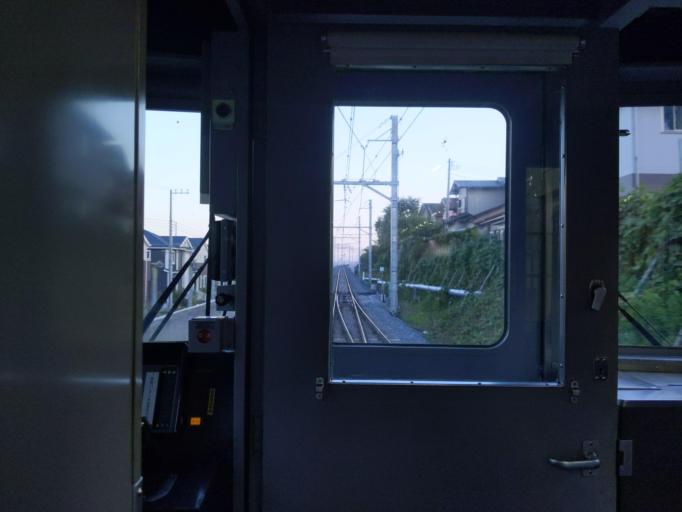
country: JP
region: Chiba
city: Noda
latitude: 35.9571
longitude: 139.8612
